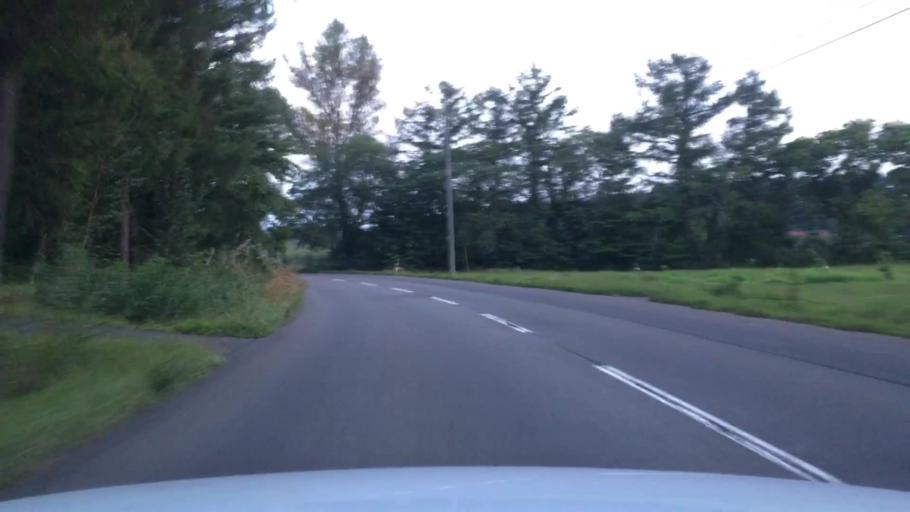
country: JP
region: Aomori
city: Shimokizukuri
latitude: 40.6875
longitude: 140.3634
